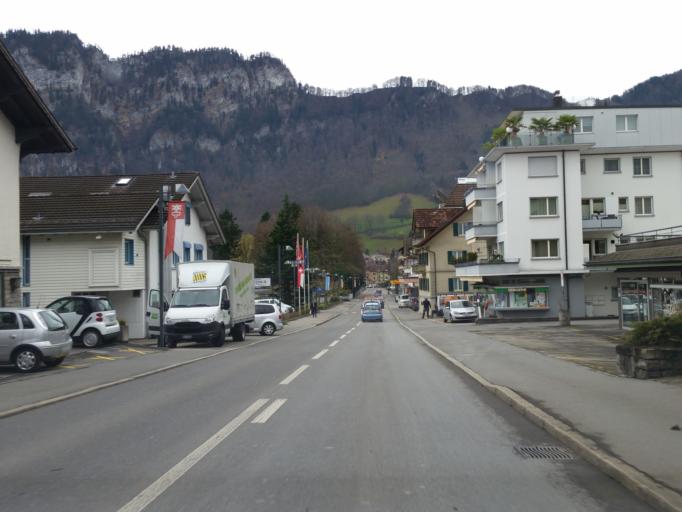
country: CH
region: Nidwalden
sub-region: Nidwalden
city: Hergiswil
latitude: 46.9899
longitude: 8.3153
